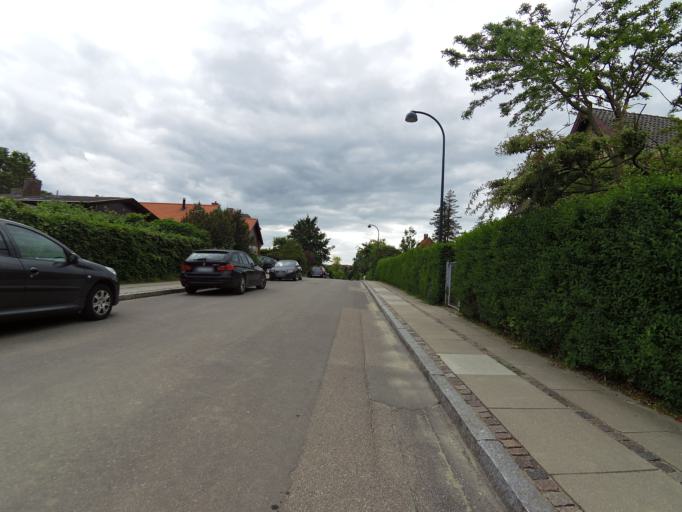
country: DK
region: Capital Region
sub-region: Frederiksberg Kommune
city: Frederiksberg
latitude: 55.7316
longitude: 12.5408
